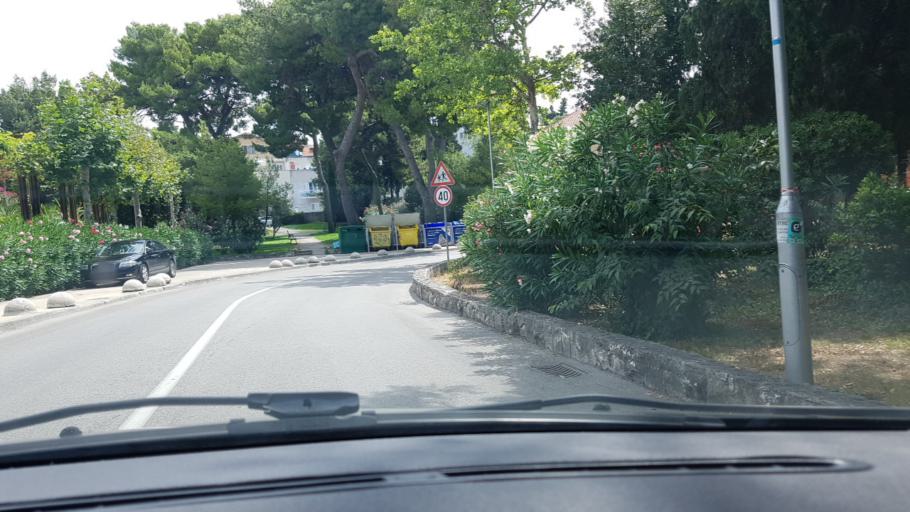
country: HR
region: Splitsko-Dalmatinska
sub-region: Grad Split
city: Split
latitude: 43.5029
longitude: 16.4478
